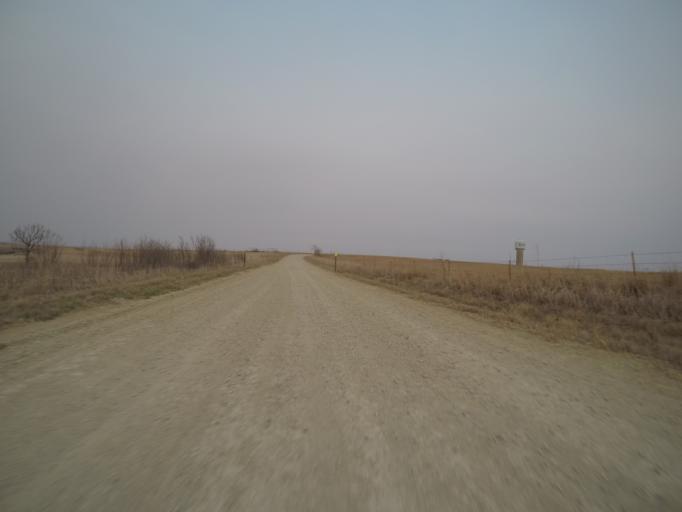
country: US
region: Kansas
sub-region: Riley County
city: Manhattan
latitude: 39.2328
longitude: -96.6508
